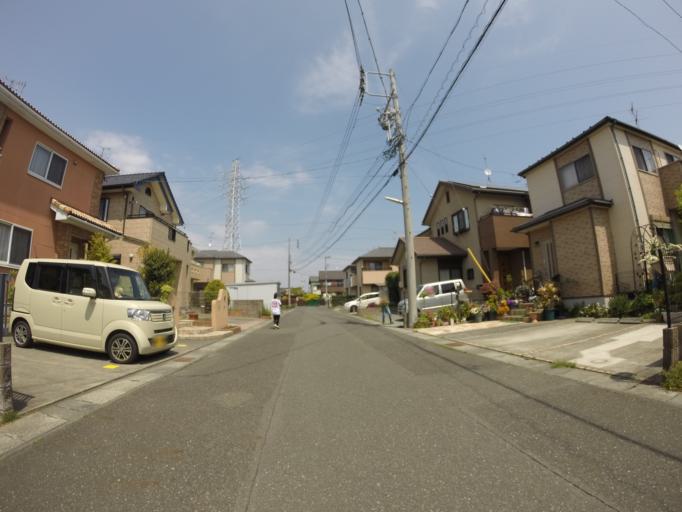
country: JP
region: Shizuoka
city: Shizuoka-shi
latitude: 34.9987
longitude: 138.5142
